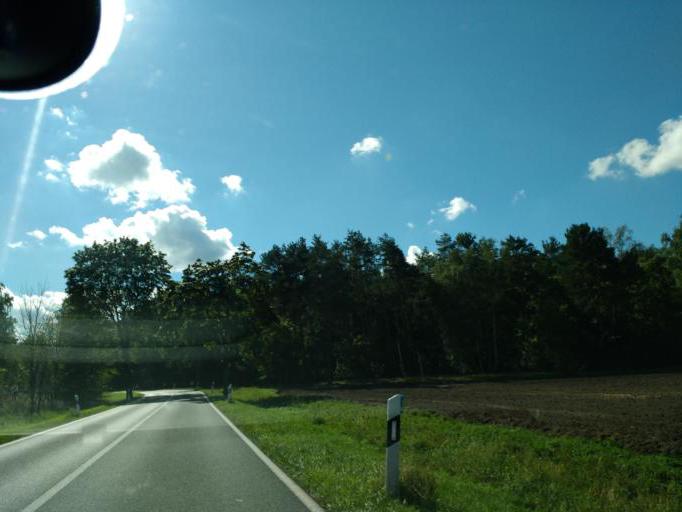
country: DE
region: Brandenburg
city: Mittenwalde
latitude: 52.2266
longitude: 13.5739
